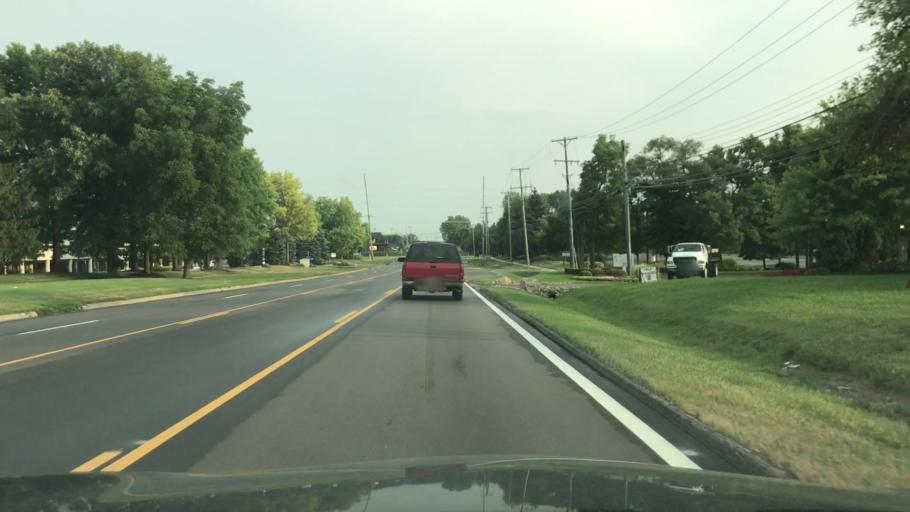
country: US
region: Michigan
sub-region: Oakland County
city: Novi
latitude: 42.4940
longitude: -83.4362
